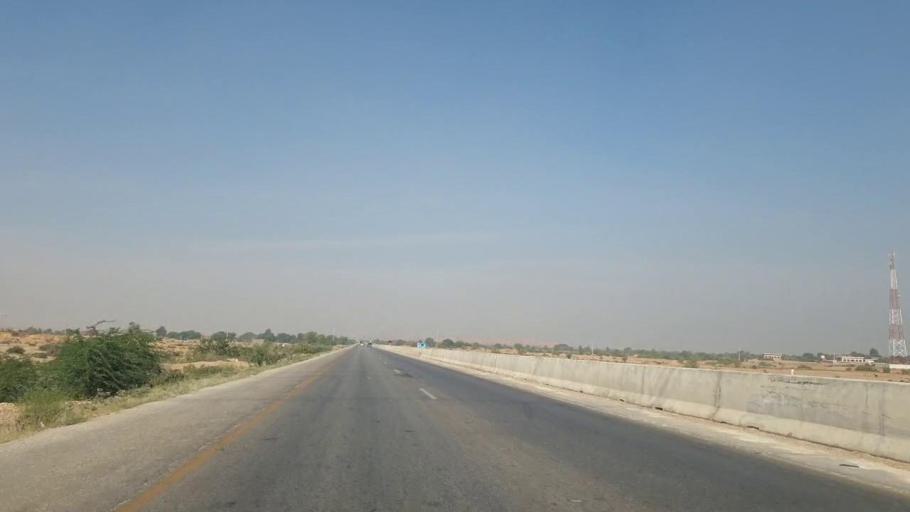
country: PK
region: Sindh
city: Matiari
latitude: 25.5885
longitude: 68.3103
